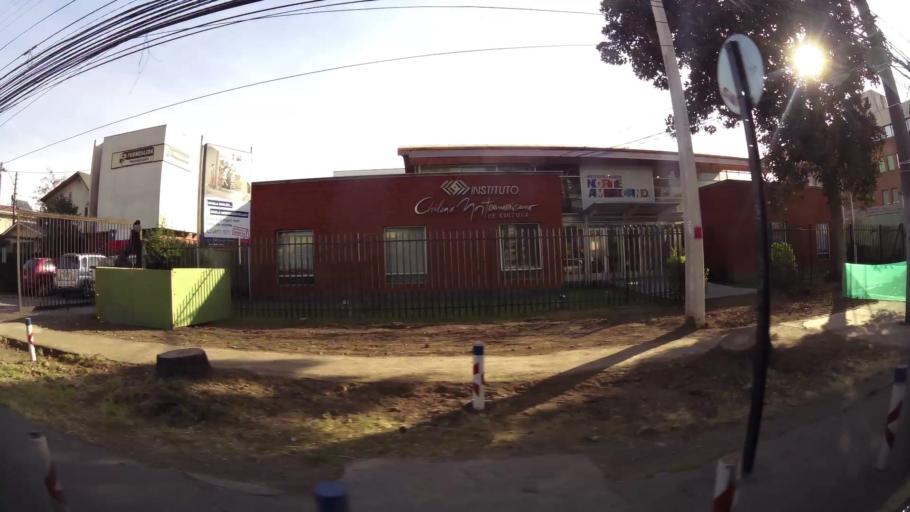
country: CL
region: Santiago Metropolitan
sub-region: Provincia de Santiago
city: Villa Presidente Frei, Nunoa, Santiago, Chile
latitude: -33.5117
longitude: -70.6104
